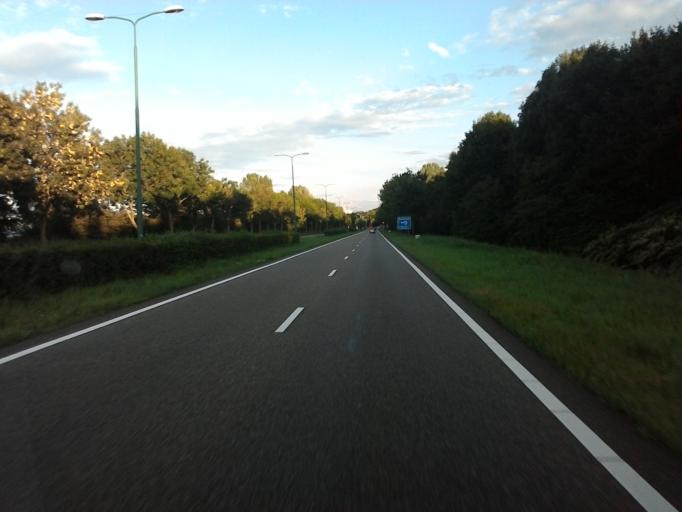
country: NL
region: Utrecht
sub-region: Stichtse Vecht
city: Maarssen
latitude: 52.1320
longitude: 5.0912
